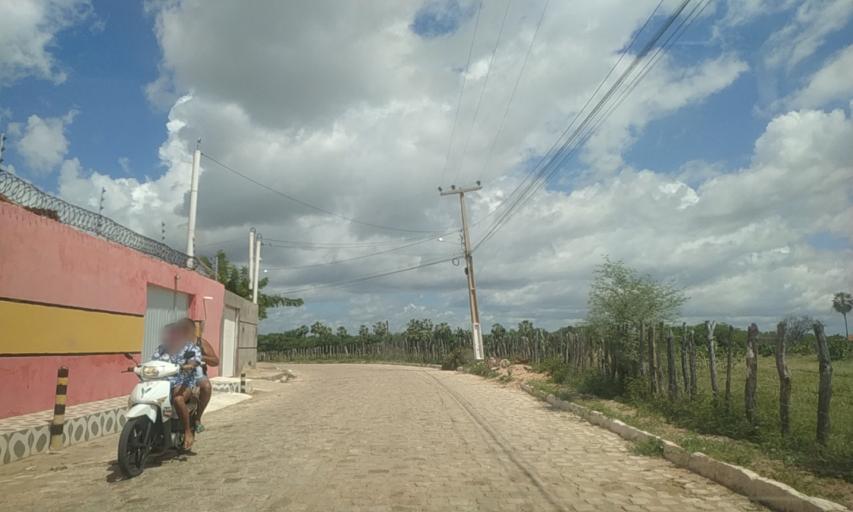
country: BR
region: Rio Grande do Norte
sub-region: Areia Branca
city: Areia Branca
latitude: -4.9306
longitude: -37.1102
